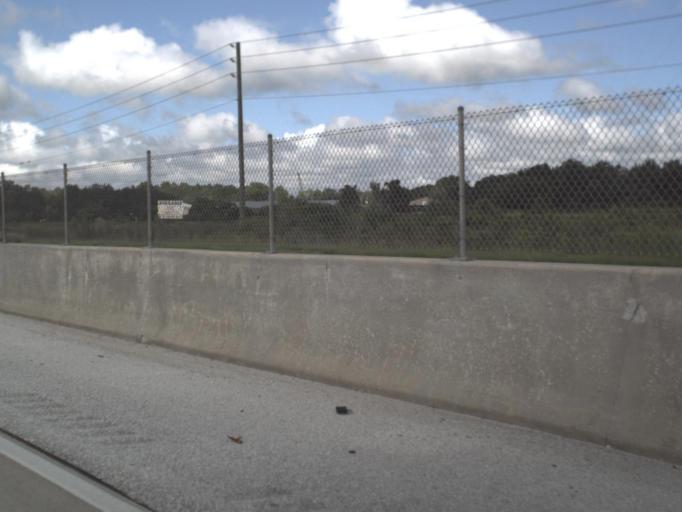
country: US
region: Florida
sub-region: Polk County
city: Winston
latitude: 28.0437
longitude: -82.0271
